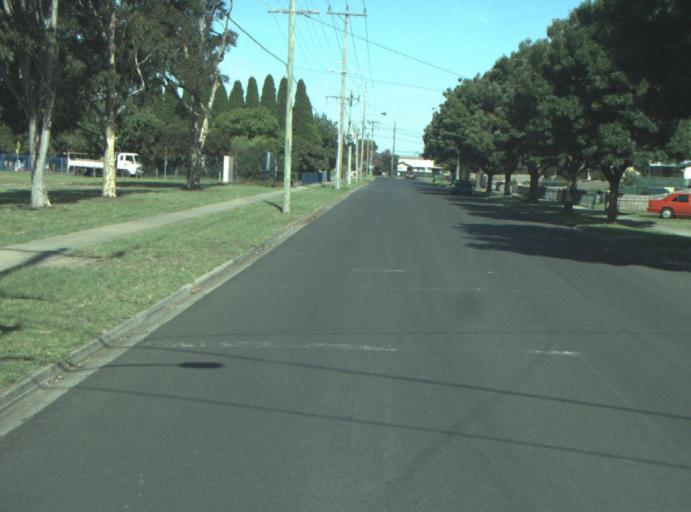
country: AU
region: Victoria
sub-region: Greater Geelong
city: Bell Park
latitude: -38.0907
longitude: 144.3505
